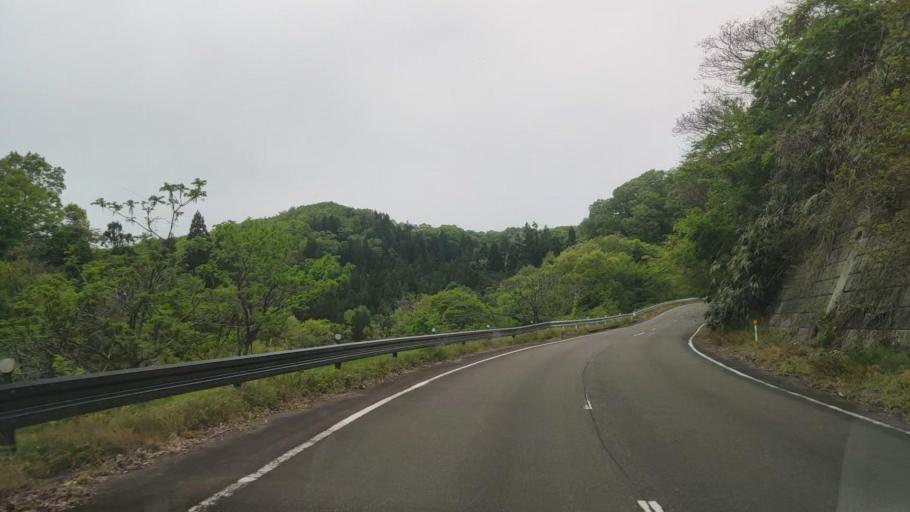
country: JP
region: Niigata
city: Kamo
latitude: 37.7109
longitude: 139.0937
